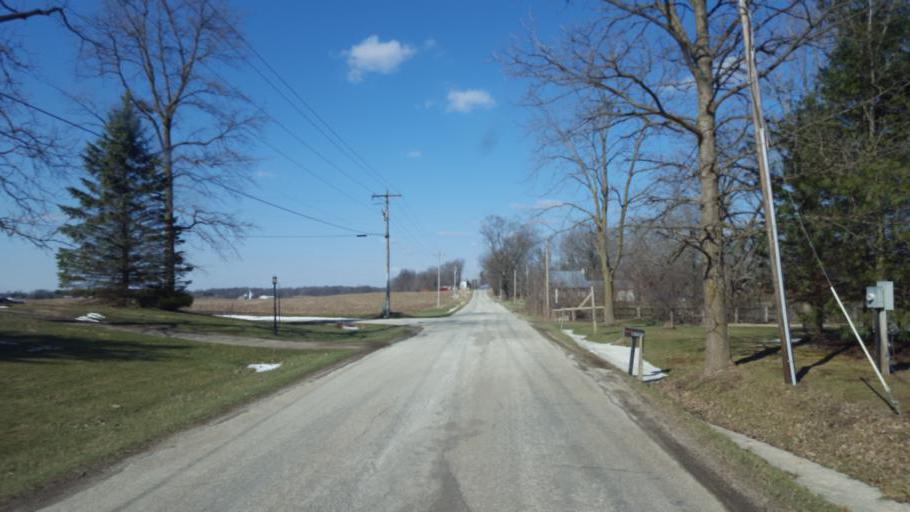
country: US
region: Ohio
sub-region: Morrow County
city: Mount Gilead
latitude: 40.4818
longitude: -82.7542
